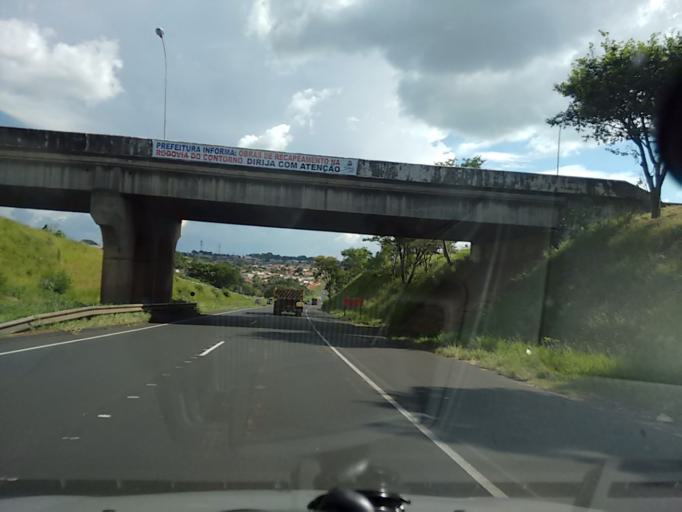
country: BR
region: Sao Paulo
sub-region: Marilia
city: Marilia
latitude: -22.2115
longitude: -49.9634
